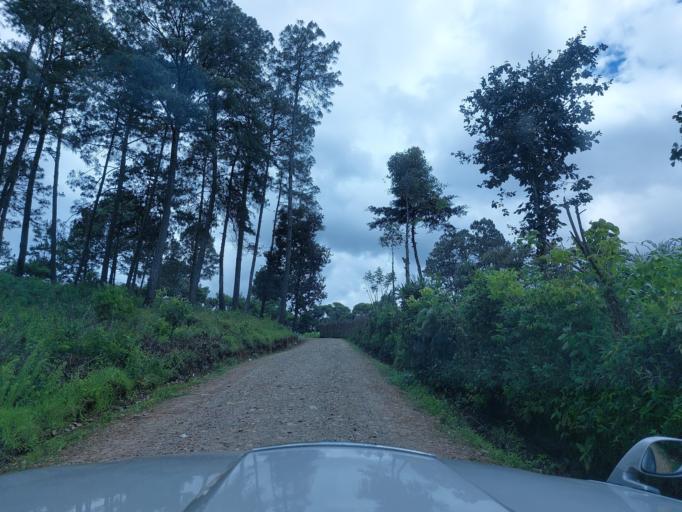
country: GT
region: Chimaltenango
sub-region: Municipio de Chimaltenango
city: Chimaltenango
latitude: 14.6465
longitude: -90.8235
